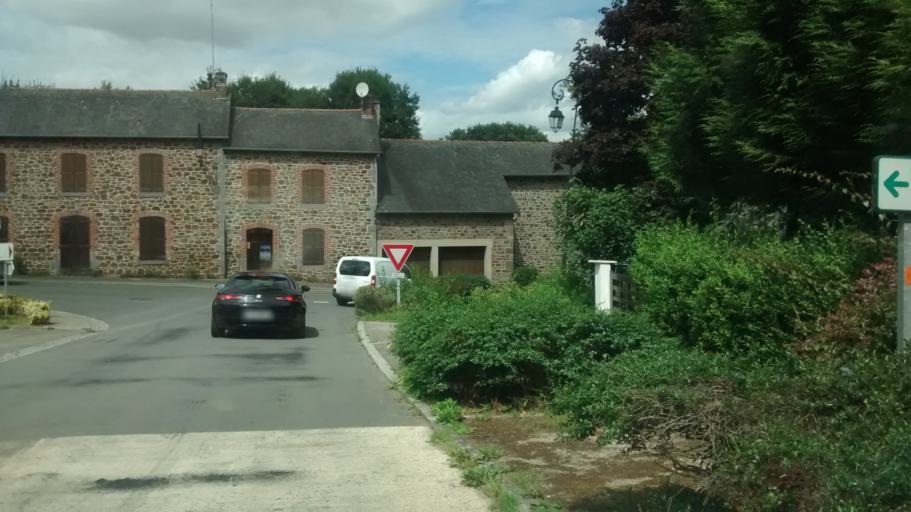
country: FR
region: Brittany
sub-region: Departement d'Ille-et-Vilaine
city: Tinteniac
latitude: 48.2917
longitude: -1.8505
